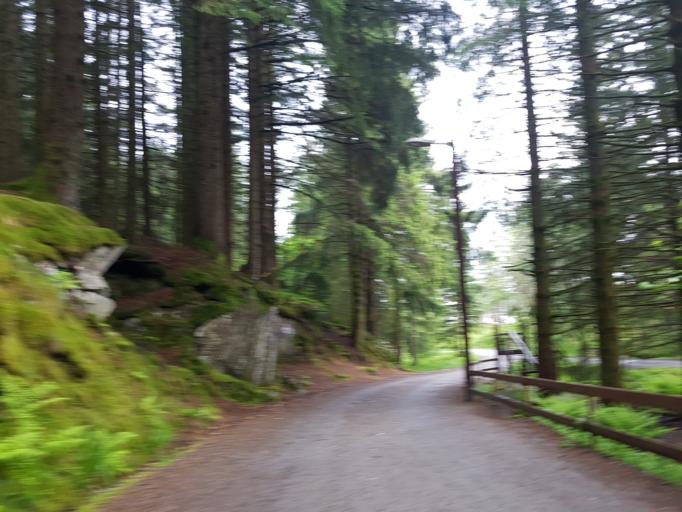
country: NO
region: Hordaland
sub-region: Bergen
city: Bergen
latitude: 60.3965
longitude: 5.3444
